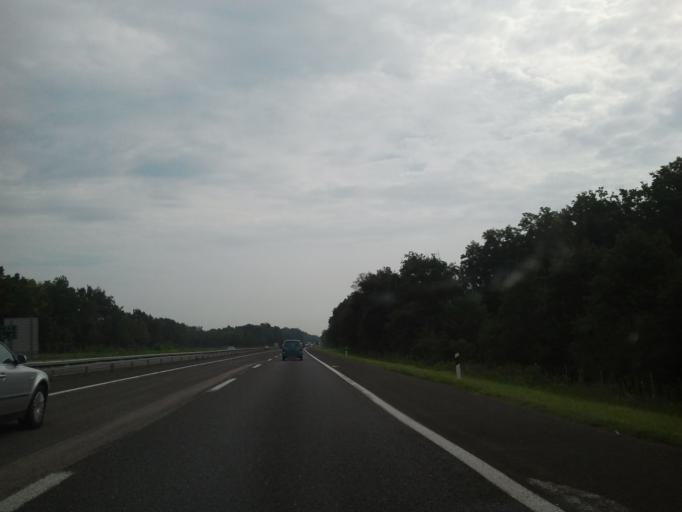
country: HR
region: Zagrebacka
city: Jastrebarsko
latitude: 45.6660
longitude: 15.7212
